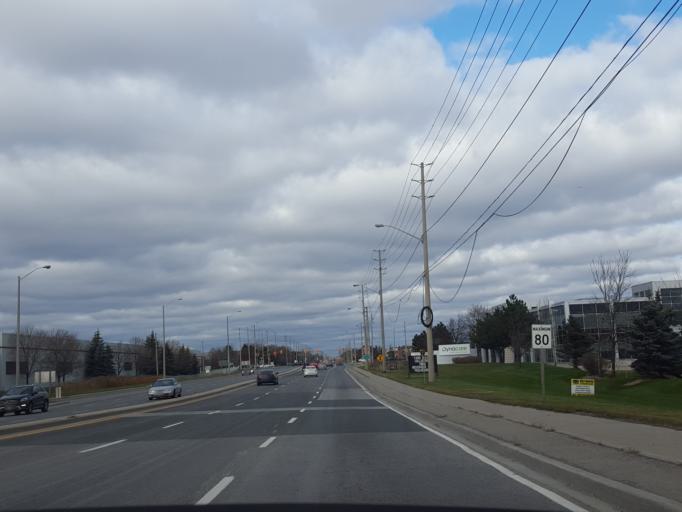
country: CA
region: Ontario
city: Brampton
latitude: 43.7283
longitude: -79.6752
